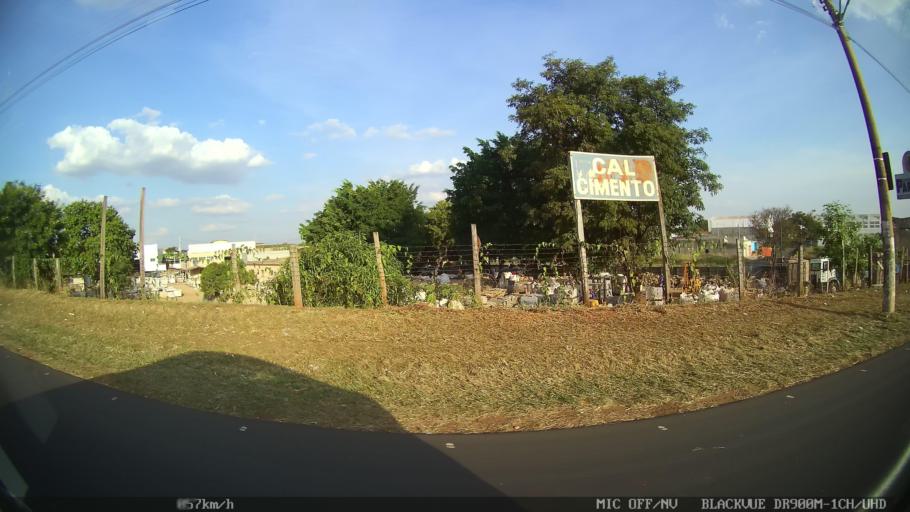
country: BR
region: Sao Paulo
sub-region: Ribeirao Preto
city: Ribeirao Preto
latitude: -21.1306
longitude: -47.7930
